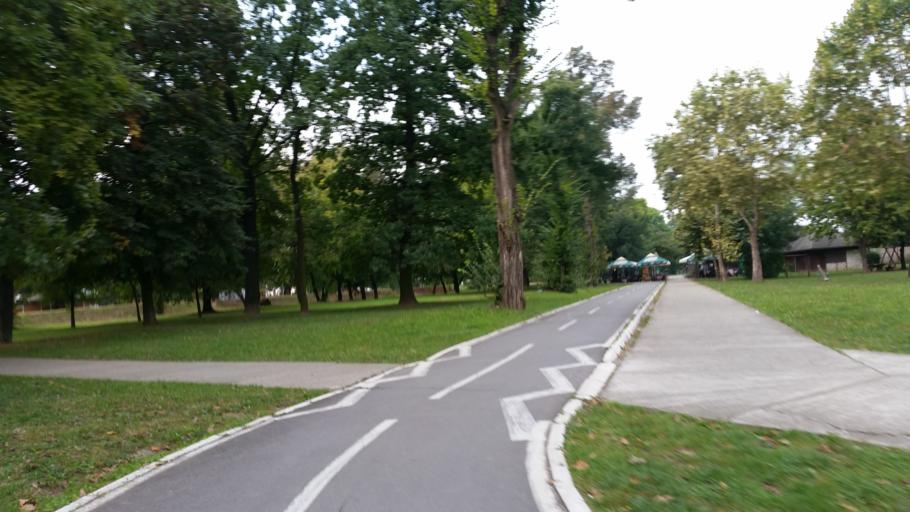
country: RS
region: Central Serbia
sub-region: Belgrade
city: Cukarica
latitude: 44.7896
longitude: 20.4058
